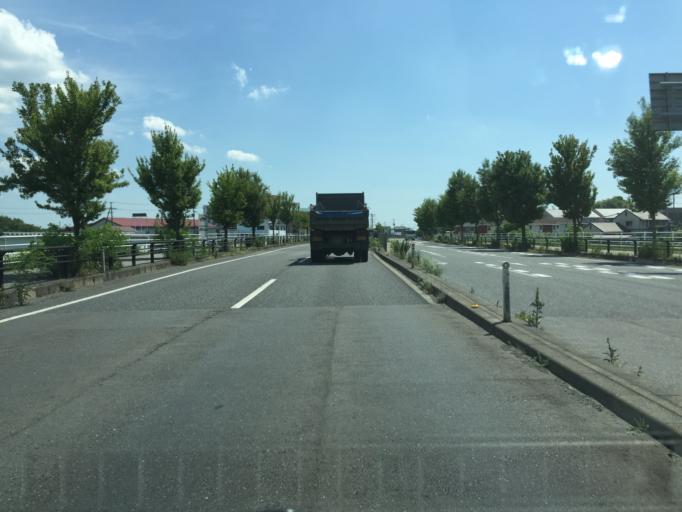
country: JP
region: Fukushima
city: Motomiya
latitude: 37.5048
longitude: 140.3937
